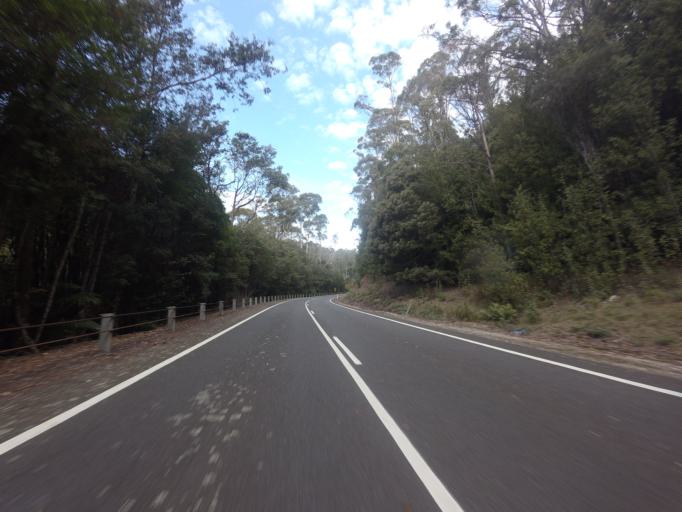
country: AU
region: Tasmania
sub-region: Meander Valley
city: Deloraine
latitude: -41.6454
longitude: 146.7191
